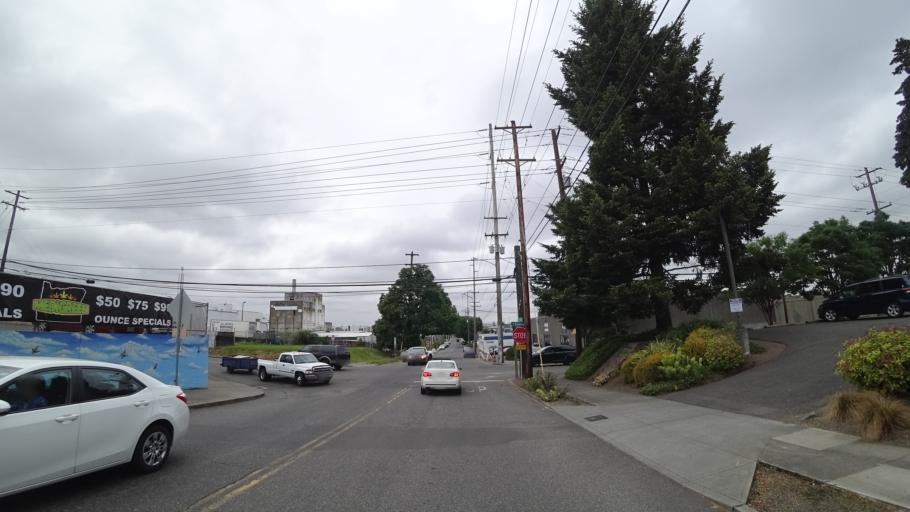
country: US
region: Oregon
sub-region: Multnomah County
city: Portland
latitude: 45.5019
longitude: -122.6578
